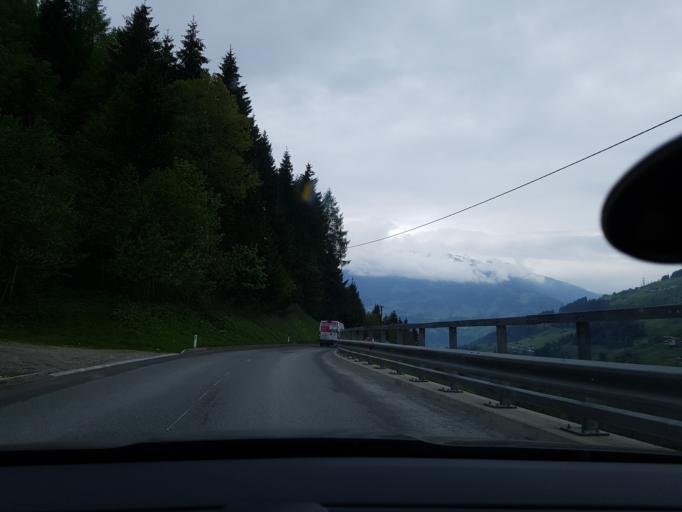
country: AT
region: Tyrol
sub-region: Politischer Bezirk Schwaz
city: Gerlosberg
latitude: 47.2120
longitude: 11.9376
